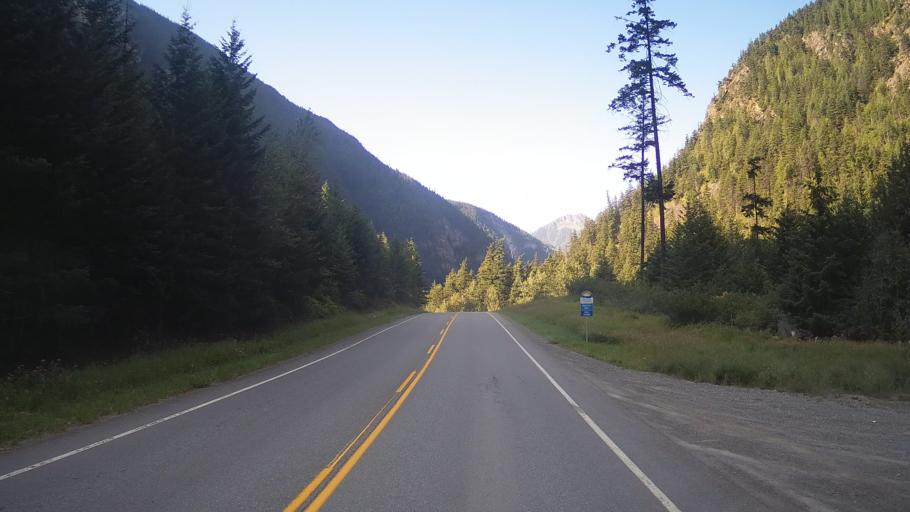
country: CA
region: British Columbia
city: Lillooet
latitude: 50.5656
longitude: -122.0901
